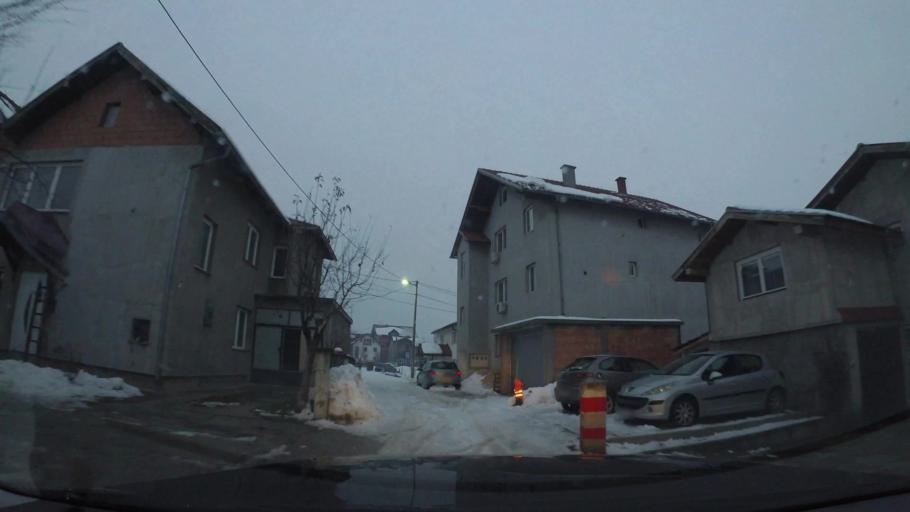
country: BA
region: Federation of Bosnia and Herzegovina
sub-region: Kanton Sarajevo
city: Sarajevo
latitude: 43.8407
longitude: 18.2921
